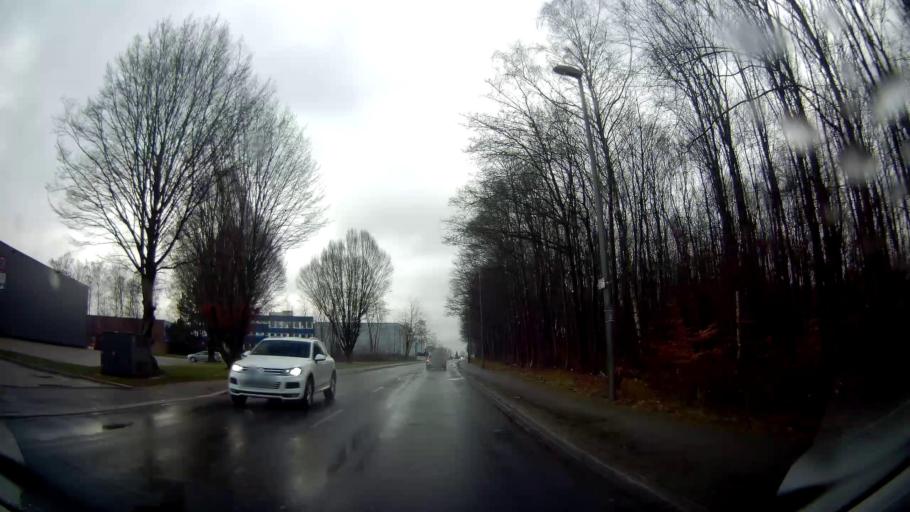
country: DE
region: North Rhine-Westphalia
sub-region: Regierungsbezirk Arnsberg
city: Herne
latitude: 51.5097
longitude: 7.2711
